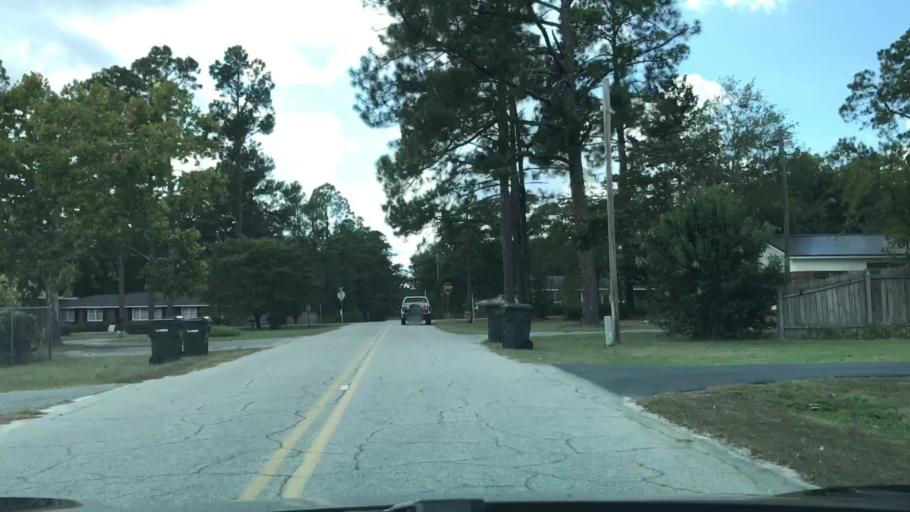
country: US
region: Georgia
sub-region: Jefferson County
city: Wadley
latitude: 32.8711
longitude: -82.3999
